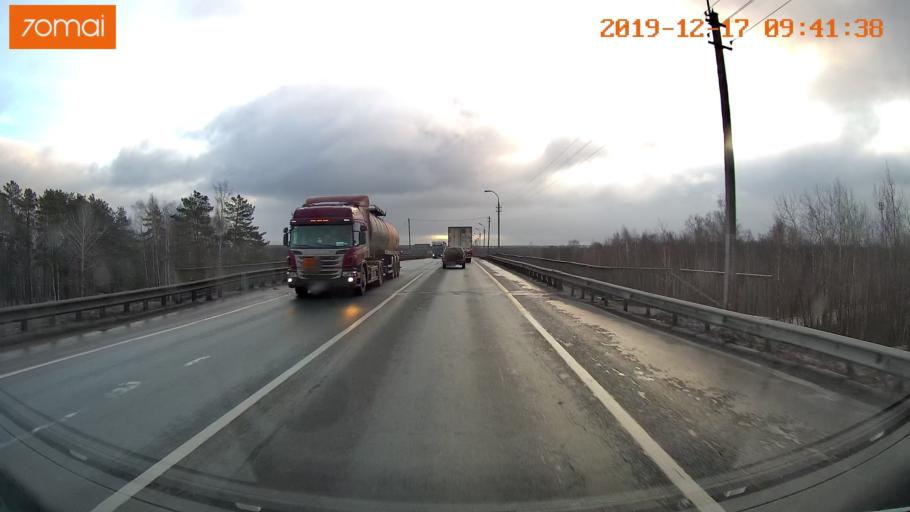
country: RU
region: Vladimir
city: Raduzhnyy
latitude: 56.0637
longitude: 40.3679
